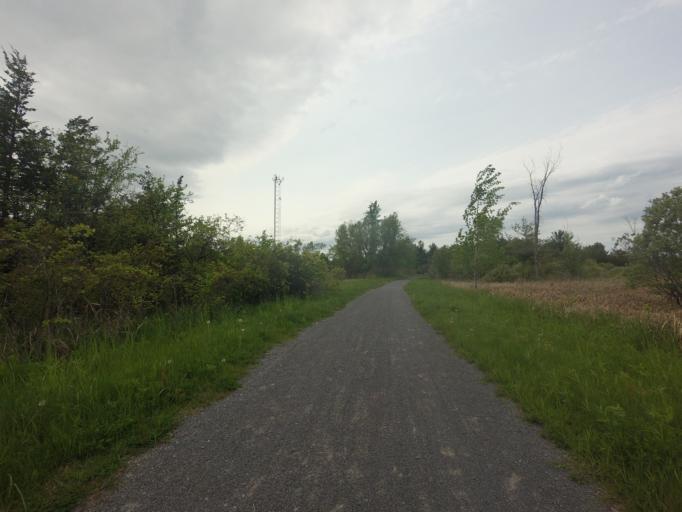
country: CA
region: Ontario
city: Kingston
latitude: 44.2807
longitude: -76.5624
